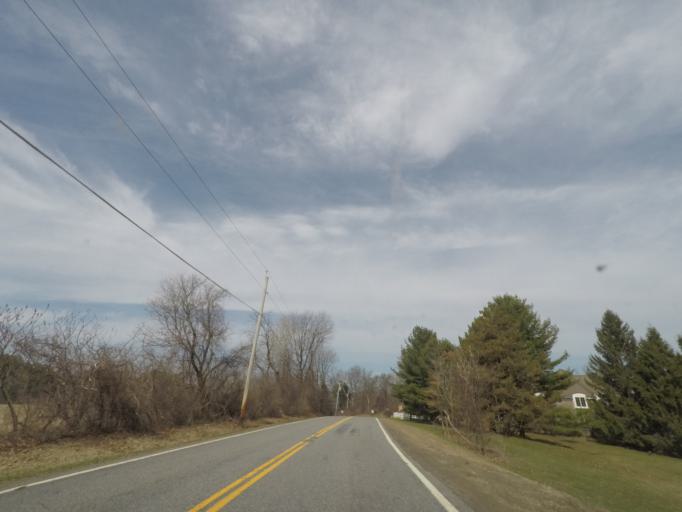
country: US
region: New York
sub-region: Saratoga County
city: Country Knolls
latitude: 42.9059
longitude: -73.7628
